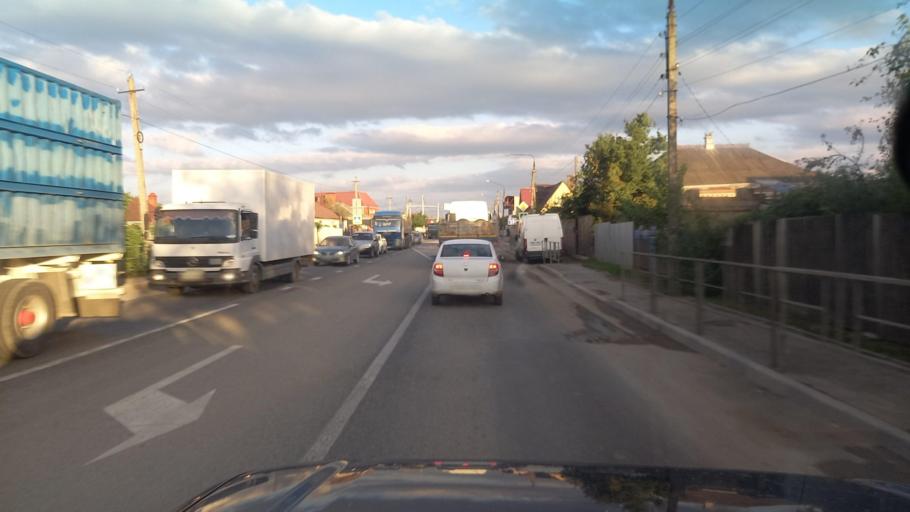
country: RU
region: Krasnodarskiy
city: Krymsk
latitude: 44.9070
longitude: 37.9707
